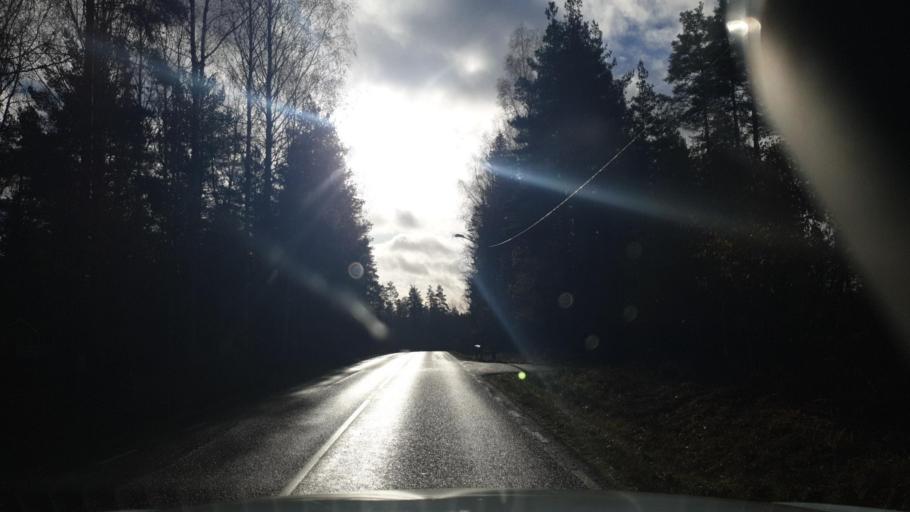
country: SE
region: Vaermland
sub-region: Grums Kommun
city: Grums
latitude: 59.4469
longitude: 12.9754
